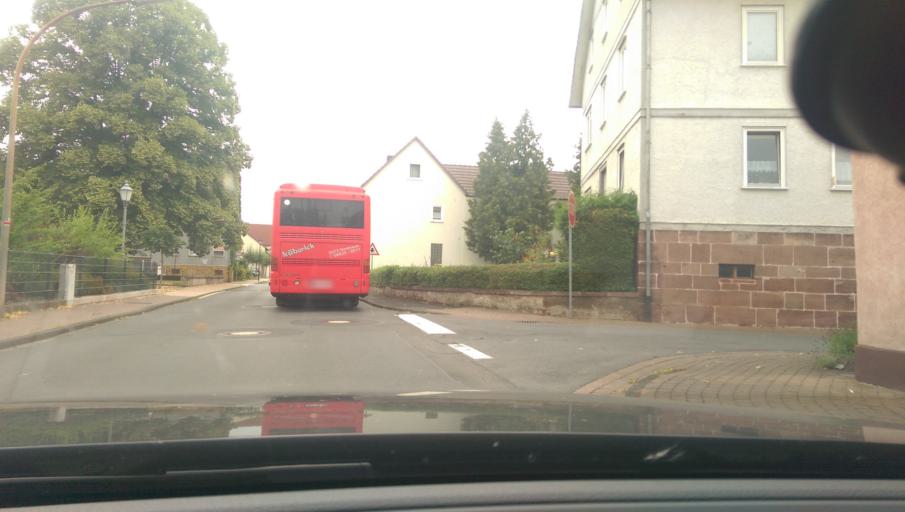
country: DE
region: Hesse
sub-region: Regierungsbezirk Kassel
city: Eschwege
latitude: 51.1518
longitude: 9.9945
